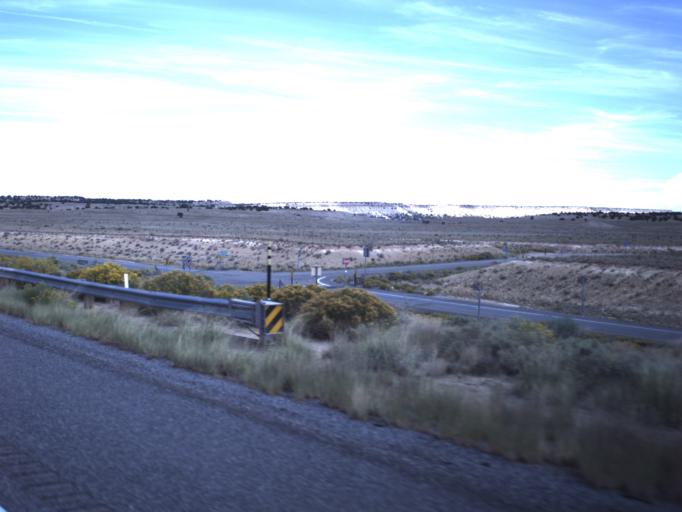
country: US
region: Utah
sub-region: Emery County
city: Castle Dale
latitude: 38.8803
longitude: -110.6595
